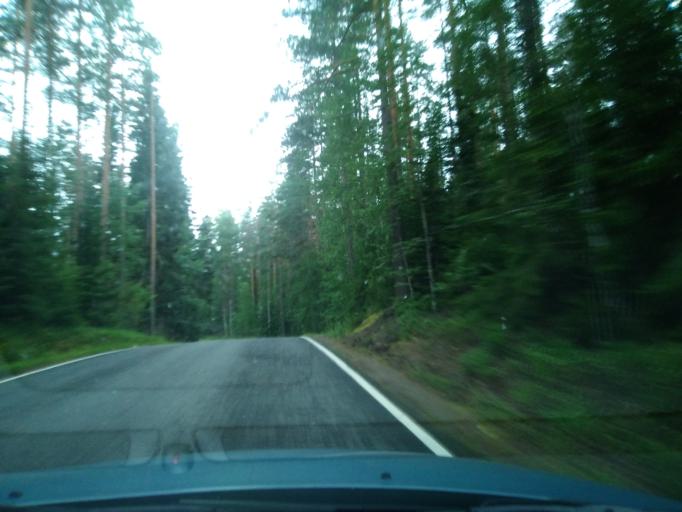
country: FI
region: Uusimaa
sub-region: Helsinki
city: Kaerkoelae
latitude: 60.7843
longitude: 24.0801
